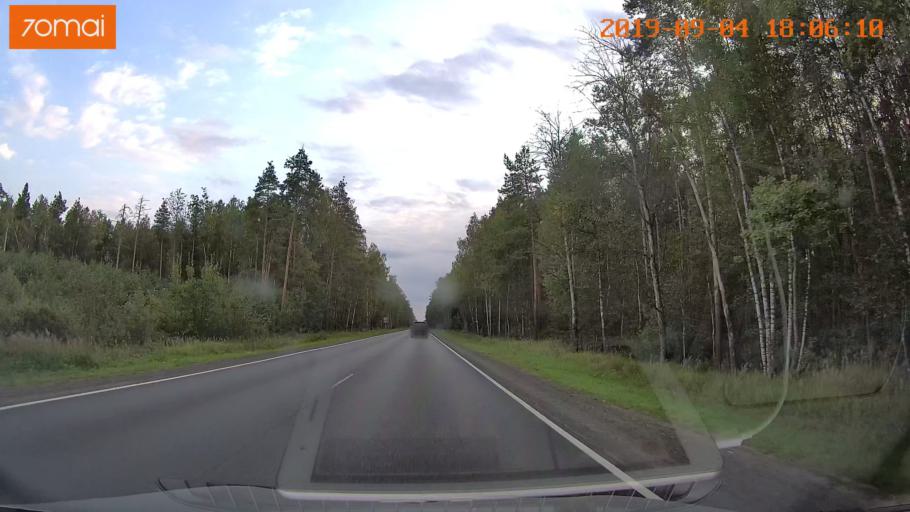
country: RU
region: Moskovskaya
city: Il'inskiy Pogost
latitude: 55.4339
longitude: 38.8180
